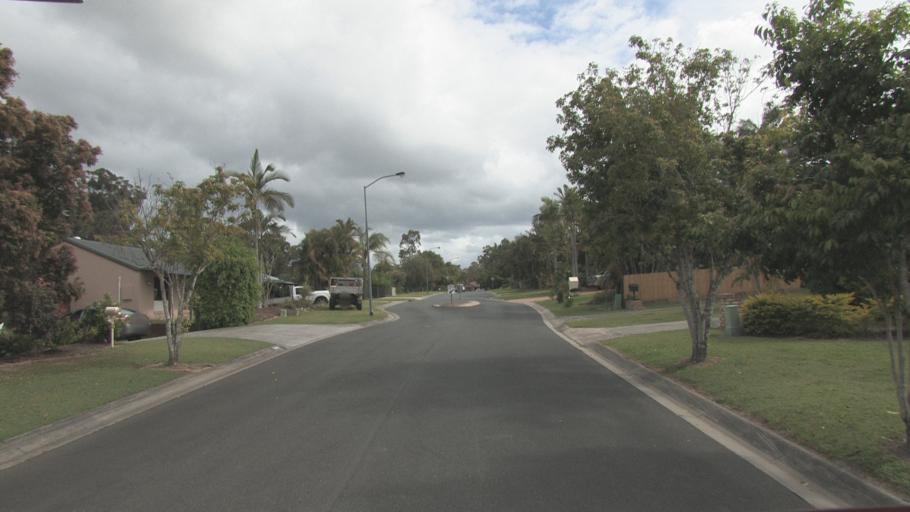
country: AU
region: Queensland
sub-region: Logan
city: Beenleigh
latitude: -27.6627
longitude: 153.2015
